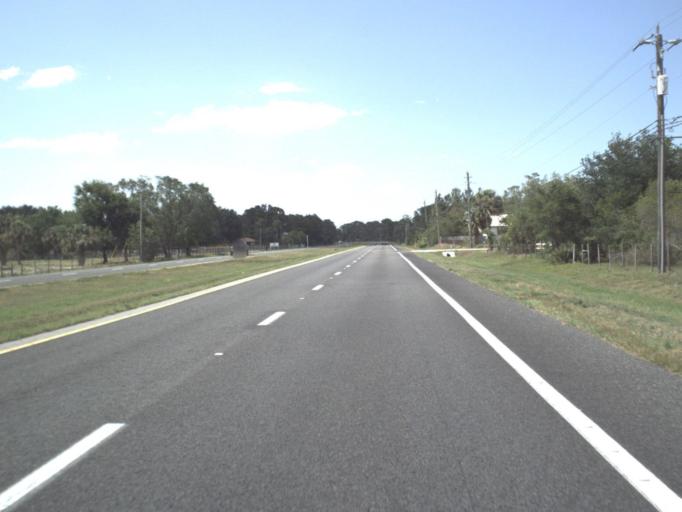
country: US
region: Florida
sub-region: Brevard County
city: Mims
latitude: 28.7382
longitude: -80.8685
